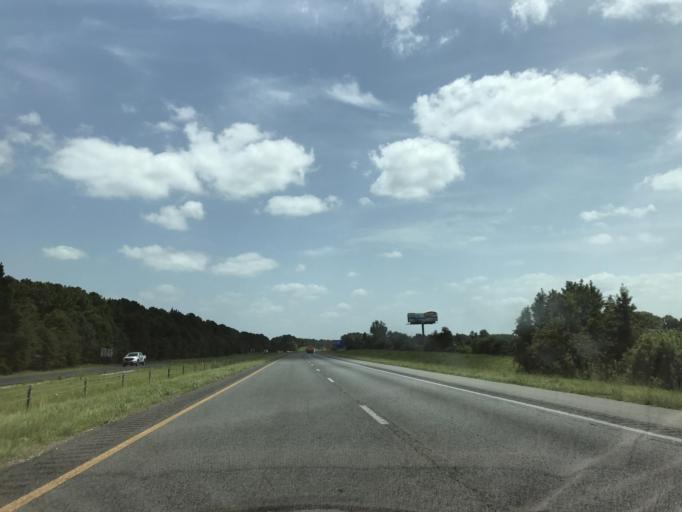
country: US
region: North Carolina
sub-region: Duplin County
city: Kenansville
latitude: 34.9247
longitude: -78.0322
